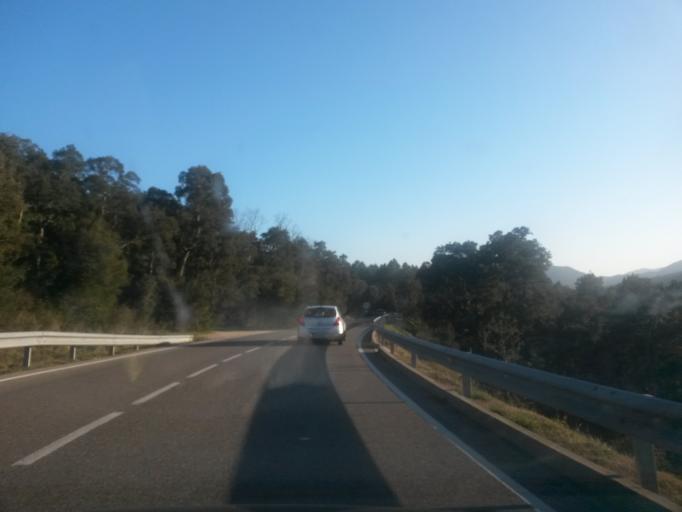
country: ES
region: Catalonia
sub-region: Provincia de Girona
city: Macanet de Cabrenys
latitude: 42.3835
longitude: 2.7874
